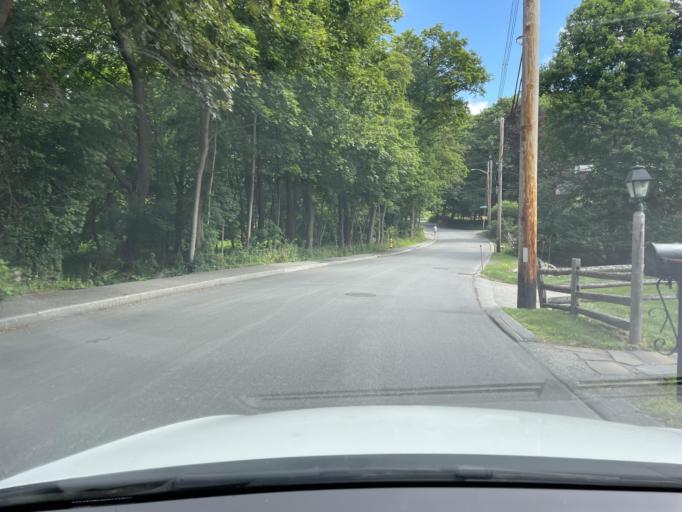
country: US
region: Massachusetts
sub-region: Essex County
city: Andover
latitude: 42.6418
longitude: -71.1251
